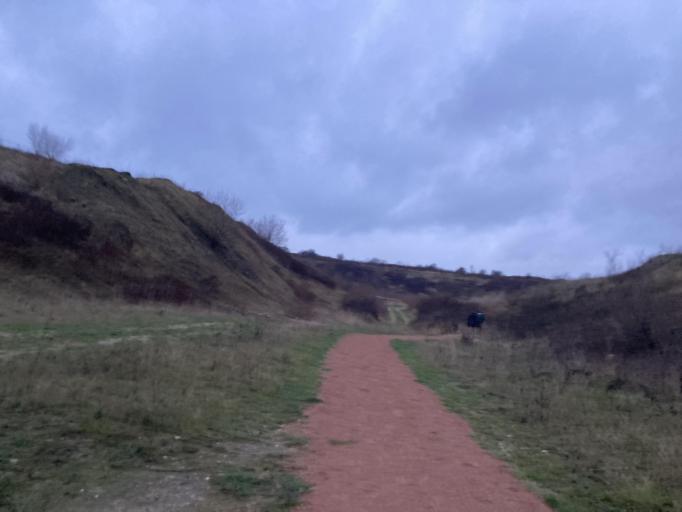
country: DK
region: Capital Region
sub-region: Hoje-Taastrup Kommune
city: Flong
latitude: 55.6765
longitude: 12.2370
